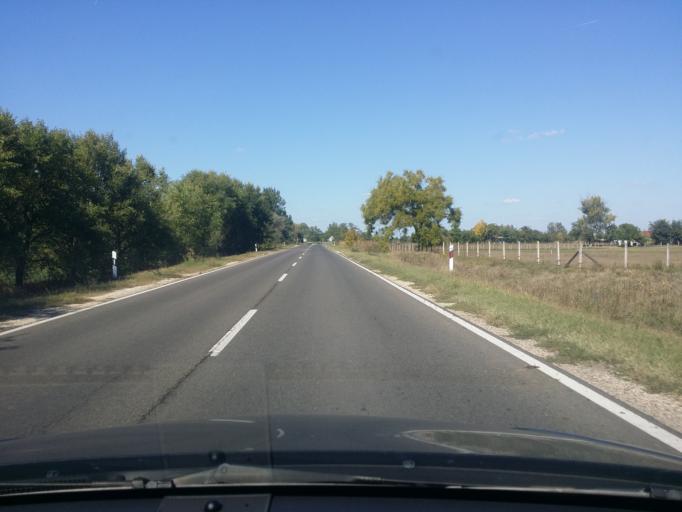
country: HU
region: Bacs-Kiskun
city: Palmonostora
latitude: 46.6332
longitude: 19.8936
